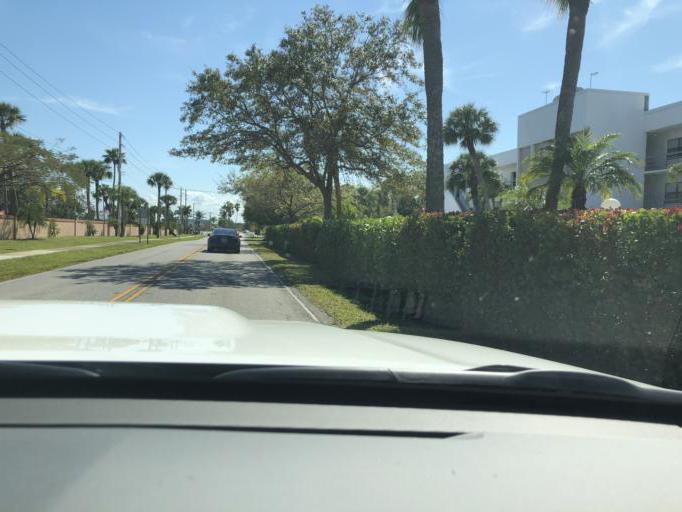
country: US
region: Florida
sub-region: Martin County
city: Palm City
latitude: 27.1780
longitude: -80.2571
